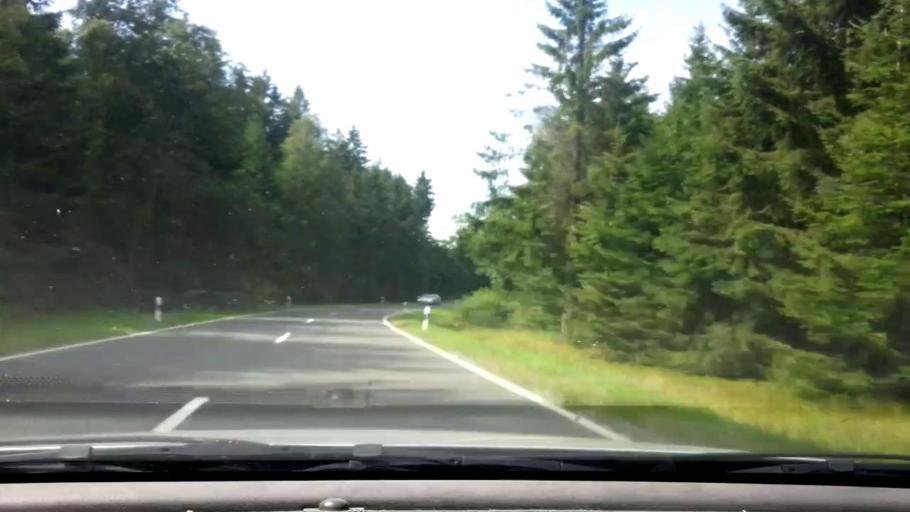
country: DE
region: Bavaria
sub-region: Upper Franconia
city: Bischofsgrun
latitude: 50.0579
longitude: 11.8277
